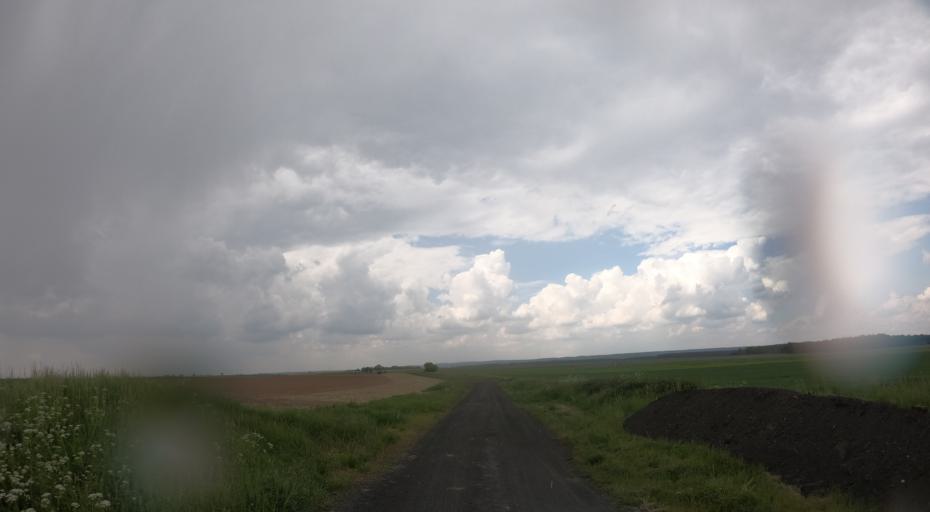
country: PL
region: West Pomeranian Voivodeship
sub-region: Powiat pyrzycki
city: Bielice
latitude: 53.2534
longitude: 14.7124
